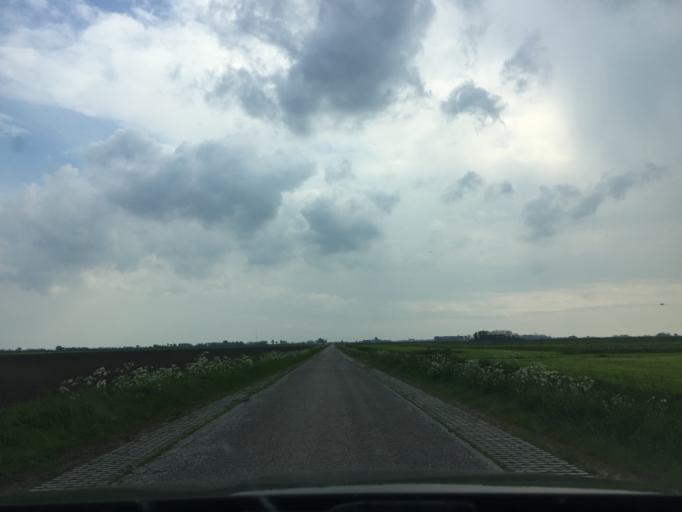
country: NL
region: Groningen
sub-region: Gemeente De Marne
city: Ulrum
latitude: 53.3350
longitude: 6.3532
